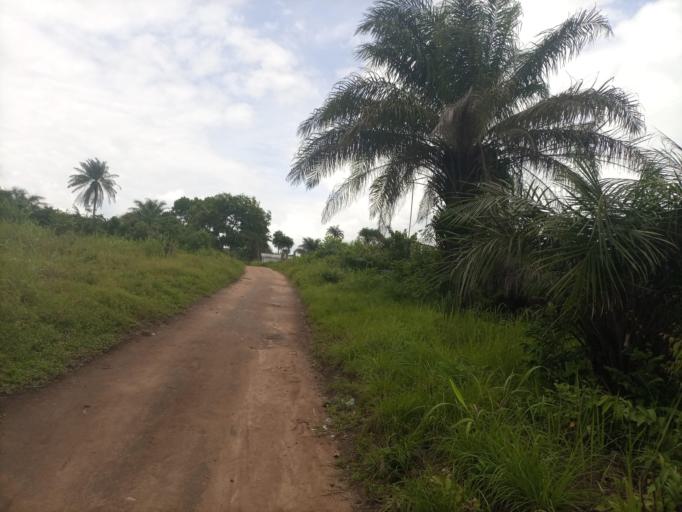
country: SL
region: Northern Province
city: Masoyila
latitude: 8.5682
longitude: -13.1558
